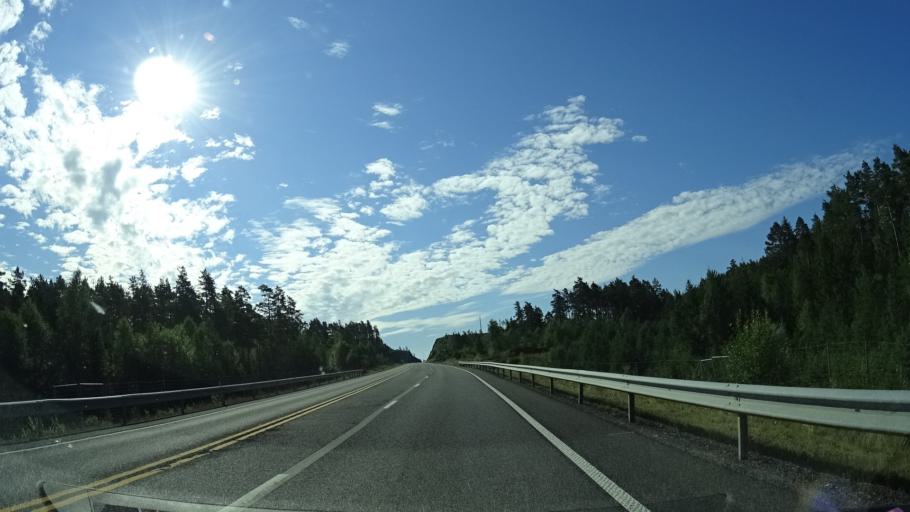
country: NO
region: Ostfold
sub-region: Marker
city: Orje
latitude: 59.5163
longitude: 11.5971
